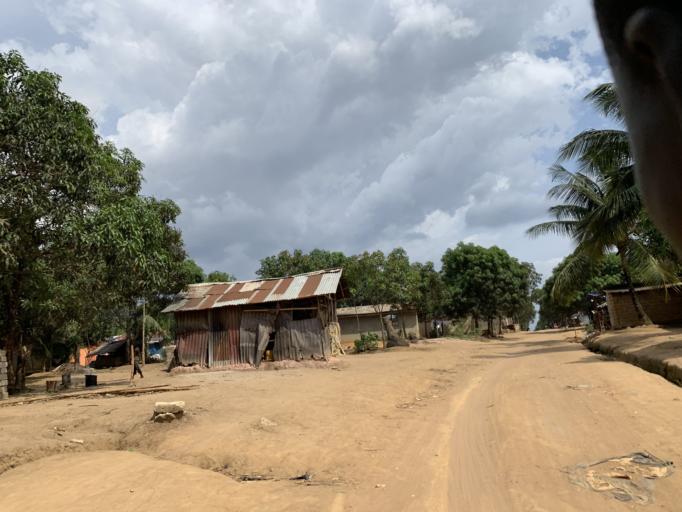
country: SL
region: Western Area
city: Waterloo
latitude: 8.3417
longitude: -13.0528
